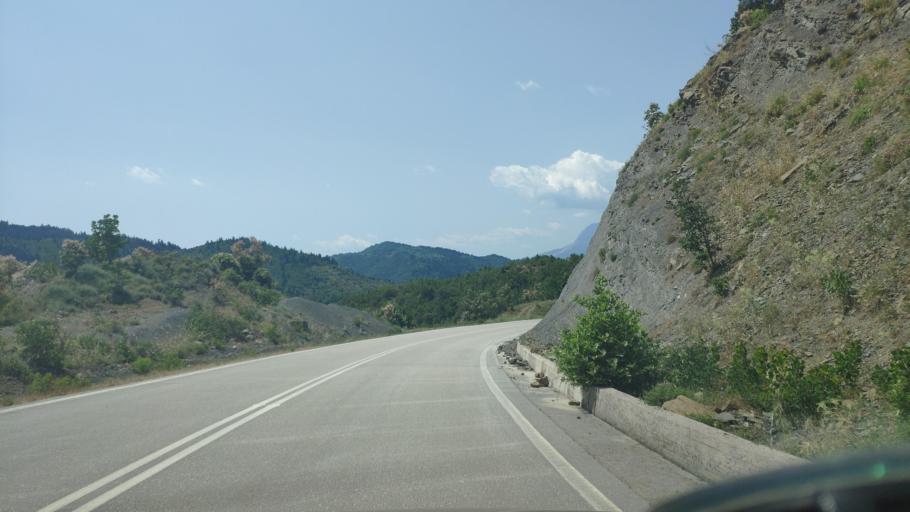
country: GR
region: Epirus
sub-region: Nomos Artas
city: Ano Kalentini
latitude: 39.2852
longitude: 21.3107
